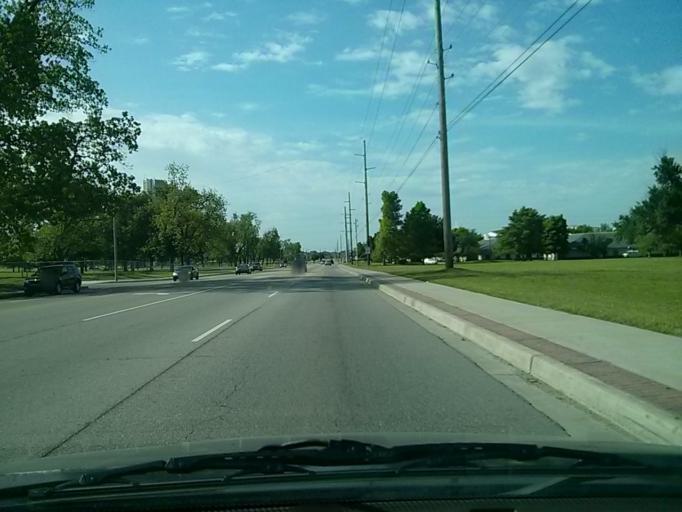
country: US
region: Oklahoma
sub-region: Tulsa County
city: Jenks
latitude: 36.0560
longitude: -95.9579
